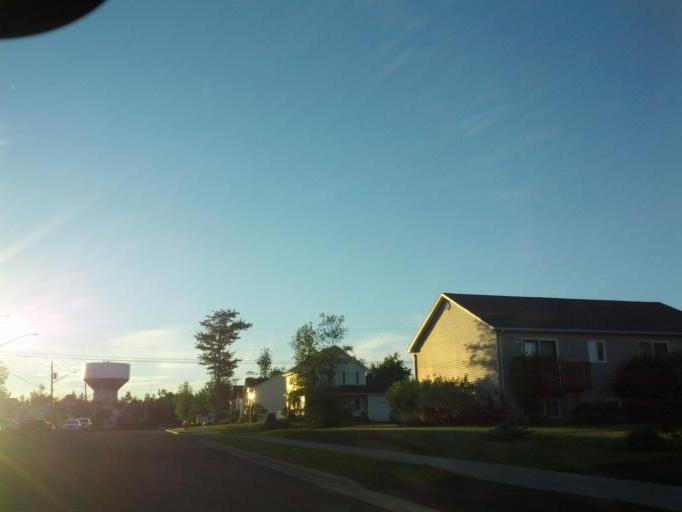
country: CA
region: New Brunswick
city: Moncton
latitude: 46.1129
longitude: -64.8654
